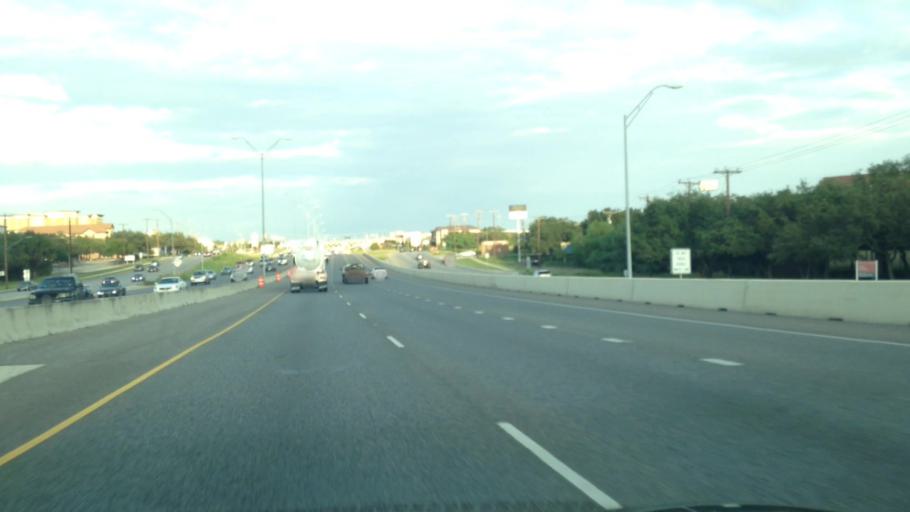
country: US
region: Texas
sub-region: Bexar County
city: Hollywood Park
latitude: 29.6076
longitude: -98.4877
